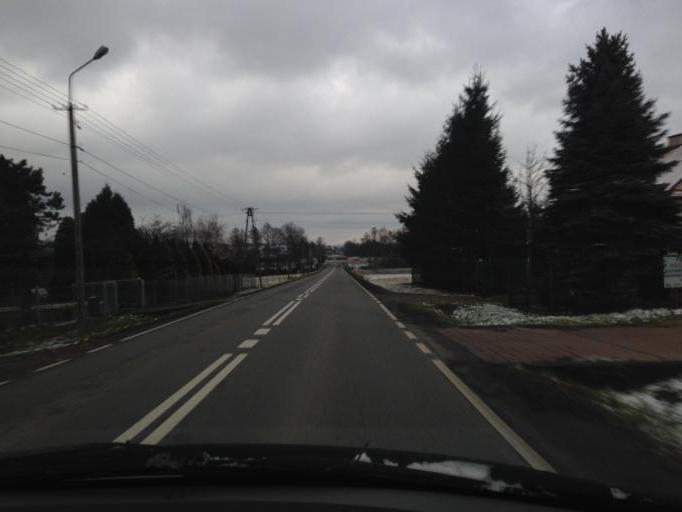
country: PL
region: Lesser Poland Voivodeship
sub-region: Powiat tarnowski
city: Janowice
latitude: 49.8553
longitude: 20.8647
